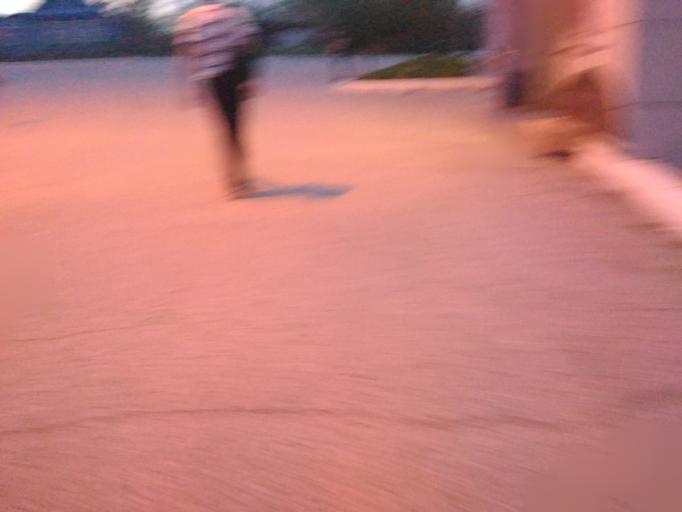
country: RU
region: Ulyanovsk
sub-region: Ulyanovskiy Rayon
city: Ulyanovsk
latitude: 54.2773
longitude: 48.3523
